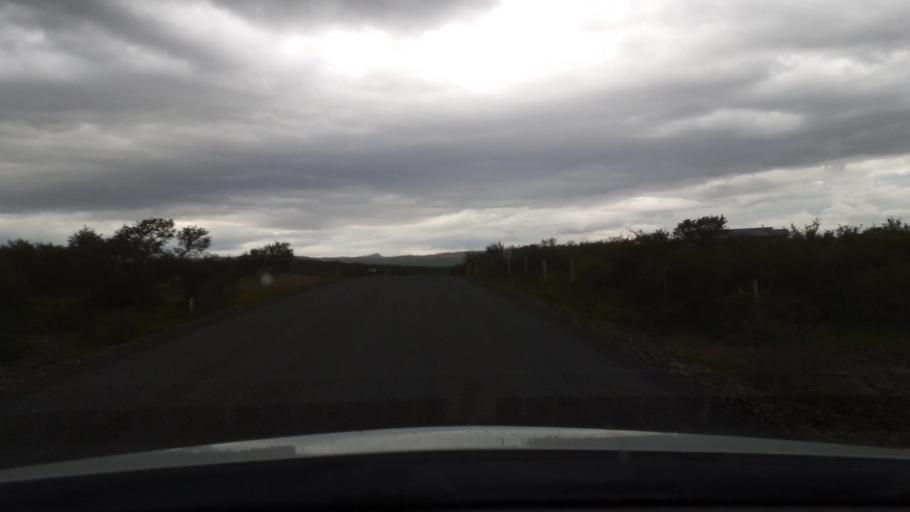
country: IS
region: West
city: Borgarnes
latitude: 64.6757
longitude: -21.7077
